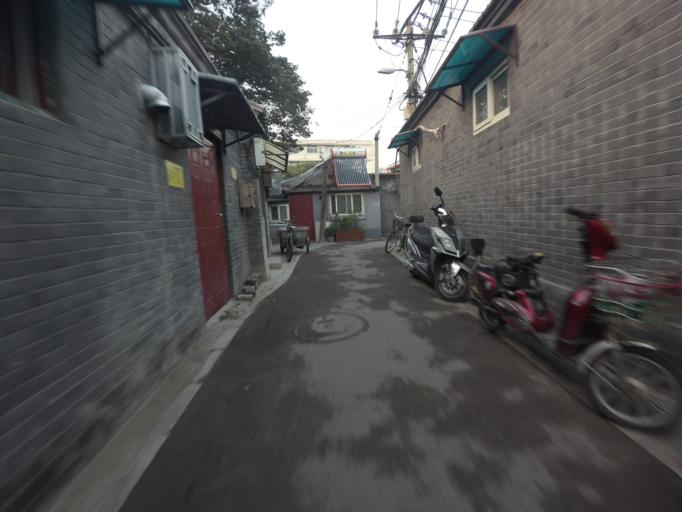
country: CN
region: Beijing
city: Jinrongjie
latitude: 39.9168
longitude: 116.3694
